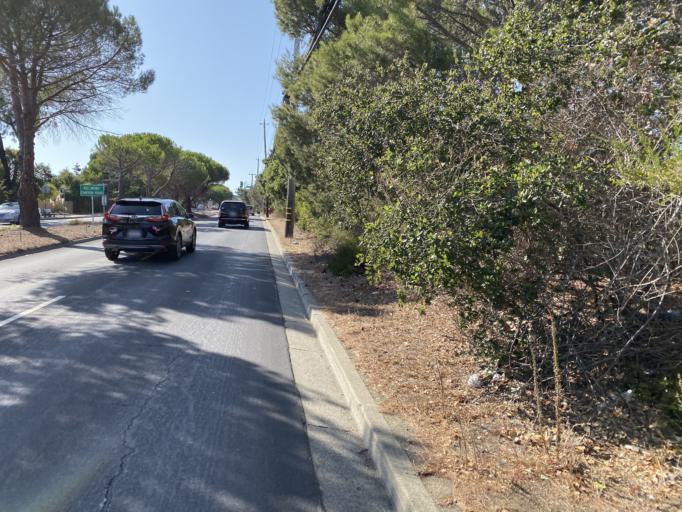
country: US
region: California
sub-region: San Mateo County
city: Highlands-Baywood Park
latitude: 37.5122
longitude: -122.3144
